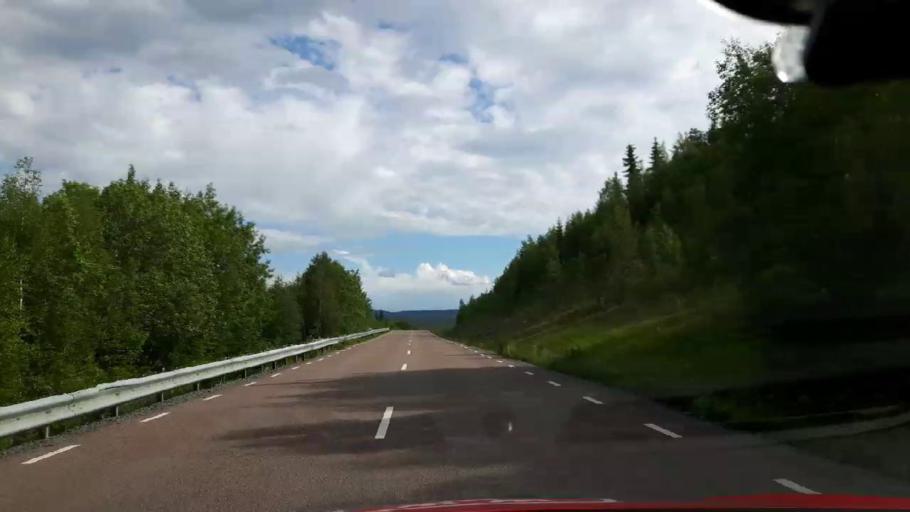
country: SE
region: Jaemtland
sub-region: Krokoms Kommun
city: Valla
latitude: 63.9269
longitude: 14.2118
